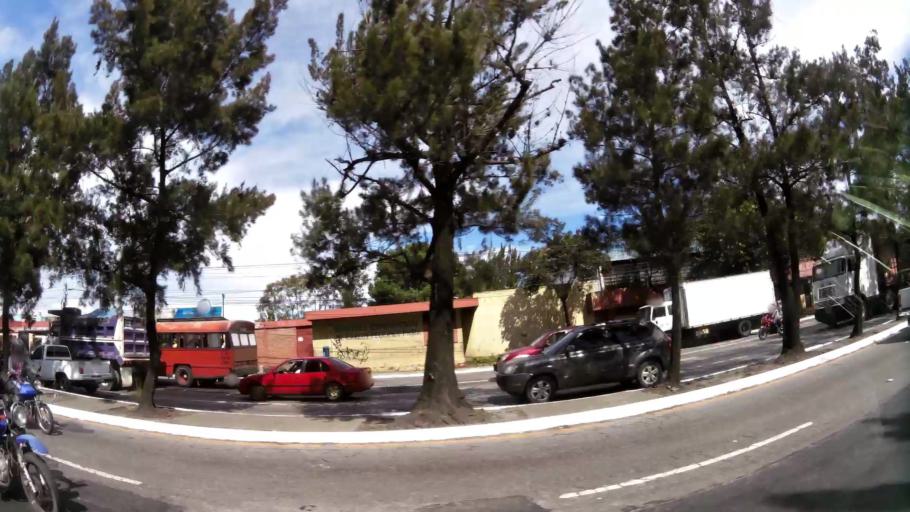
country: GT
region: Guatemala
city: Guatemala City
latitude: 14.6323
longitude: -90.5583
